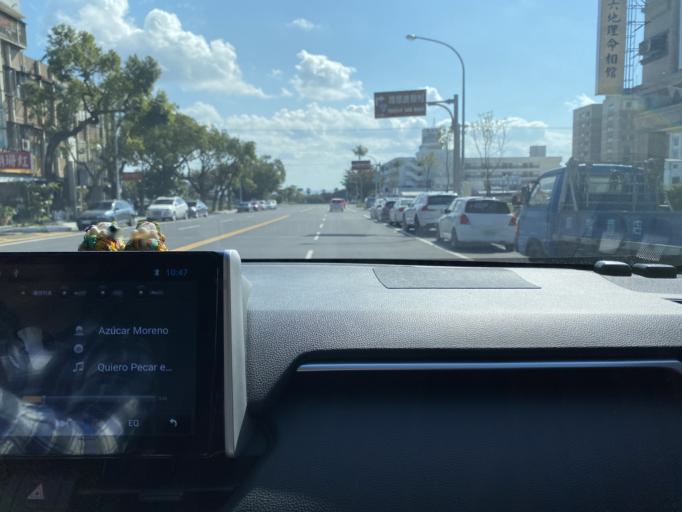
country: TW
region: Taiwan
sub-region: Hualien
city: Hualian
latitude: 23.9850
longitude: 121.6215
